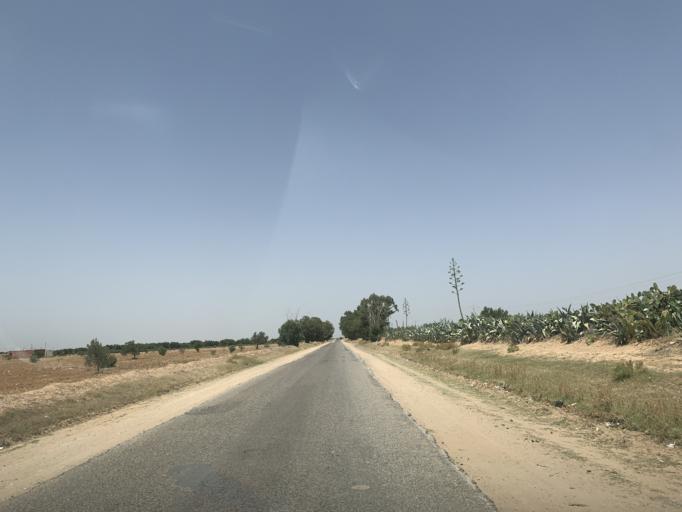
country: TN
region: Al Mahdiyah
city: Shurban
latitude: 35.1746
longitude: 10.2315
